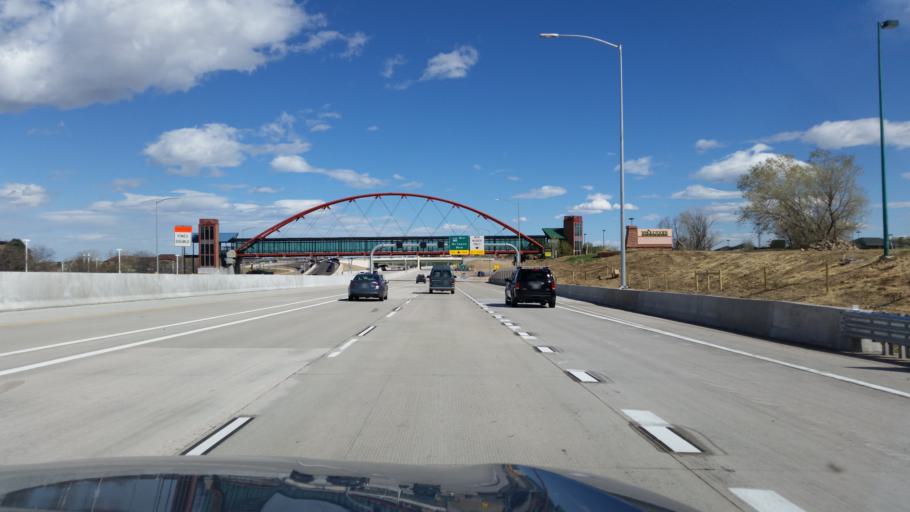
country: US
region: Colorado
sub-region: Boulder County
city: Superior
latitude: 39.9598
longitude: -105.1711
